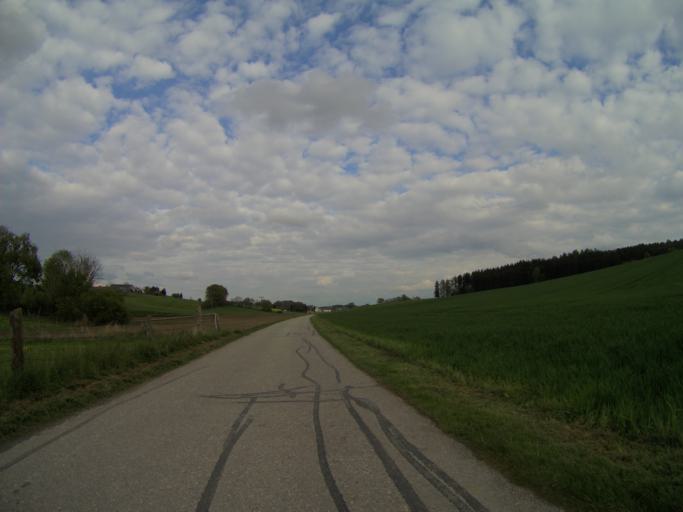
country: DE
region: Bavaria
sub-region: Upper Bavaria
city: Freising
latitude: 48.4248
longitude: 11.7585
